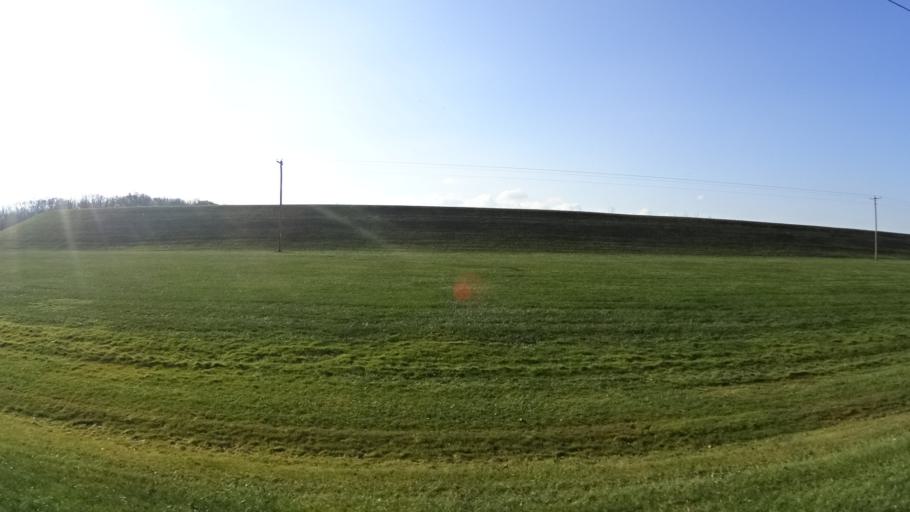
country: US
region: Ohio
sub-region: Lorain County
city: Oberlin
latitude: 41.2806
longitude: -82.1740
